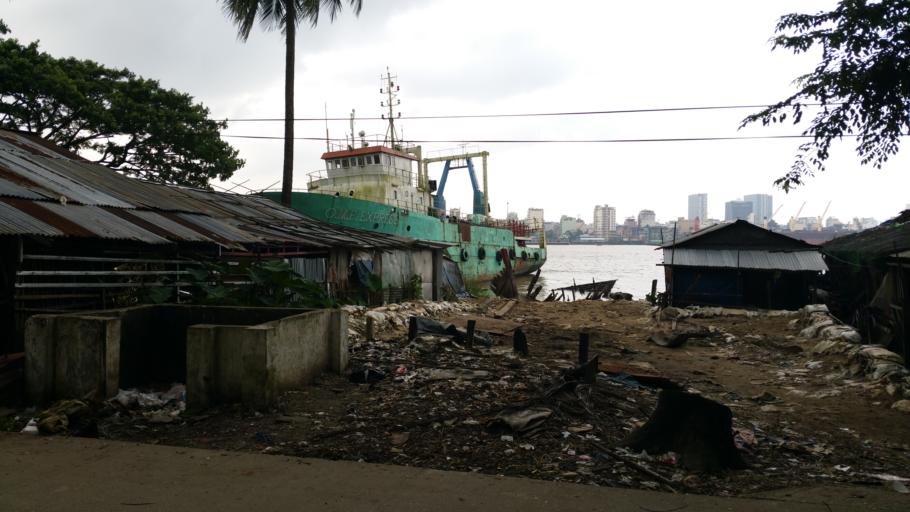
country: MM
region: Yangon
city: Yangon
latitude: 16.7646
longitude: 96.1468
